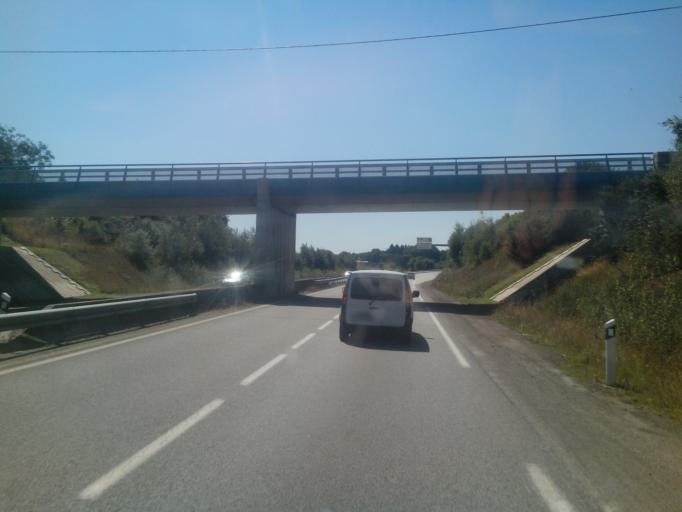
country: FR
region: Brittany
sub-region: Departement des Cotes-d'Armor
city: Loudeac
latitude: 48.1722
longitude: -2.7327
